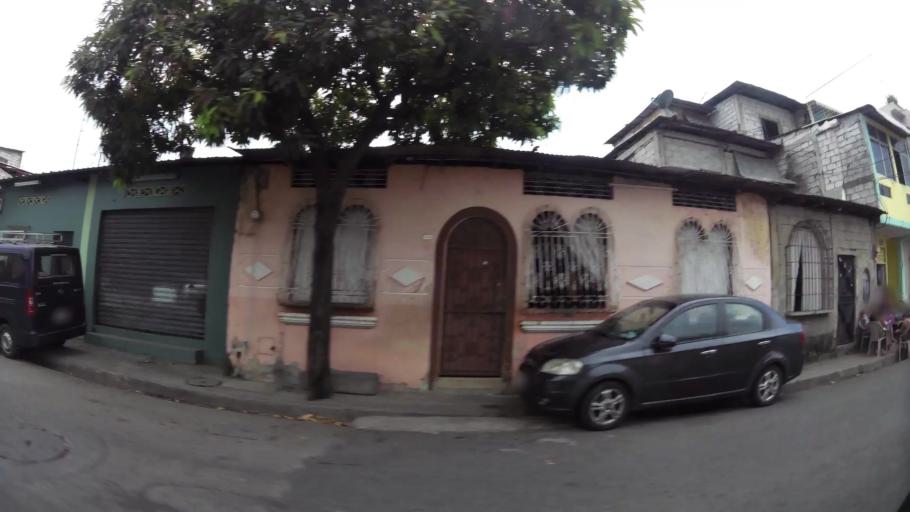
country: EC
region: Guayas
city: Guayaquil
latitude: -2.2614
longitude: -79.8871
